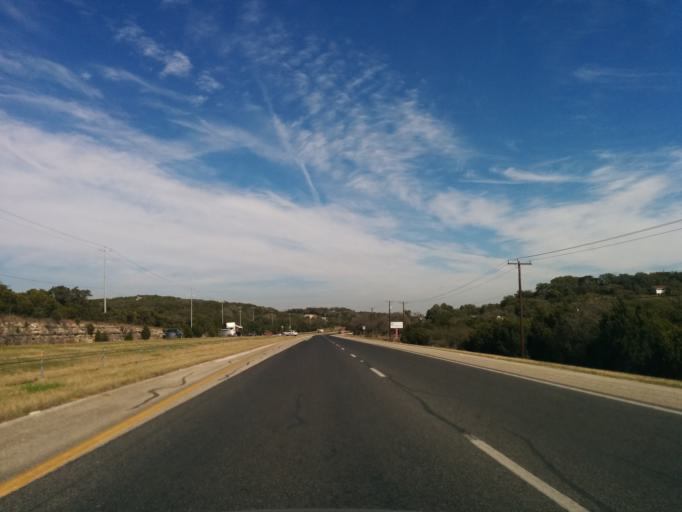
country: US
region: Texas
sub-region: Bexar County
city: Timberwood Park
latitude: 29.7026
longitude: -98.4508
